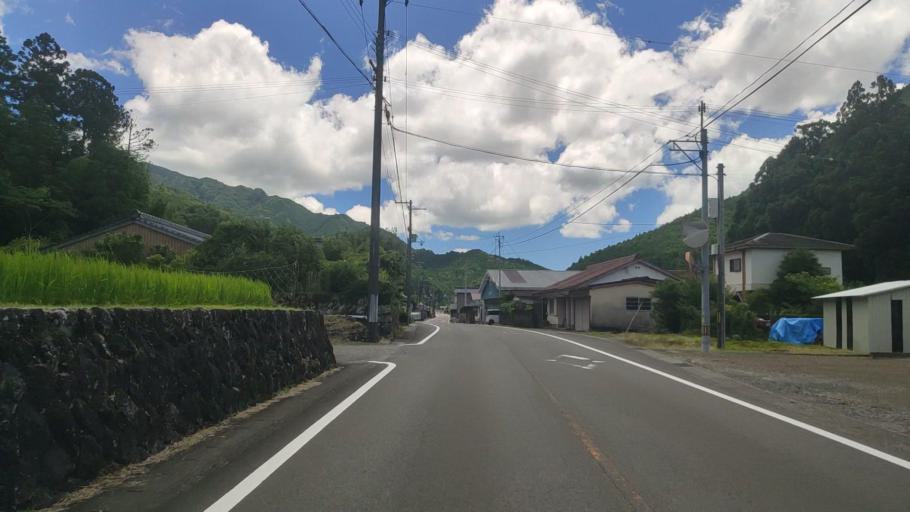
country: JP
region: Mie
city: Owase
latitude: 33.9779
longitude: 136.0527
